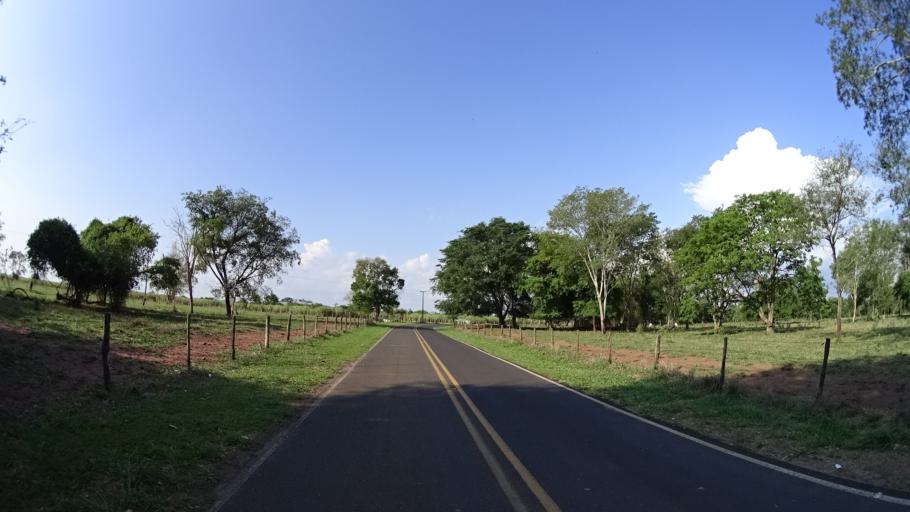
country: BR
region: Sao Paulo
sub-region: Urupes
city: Urupes
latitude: -21.3971
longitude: -49.5139
